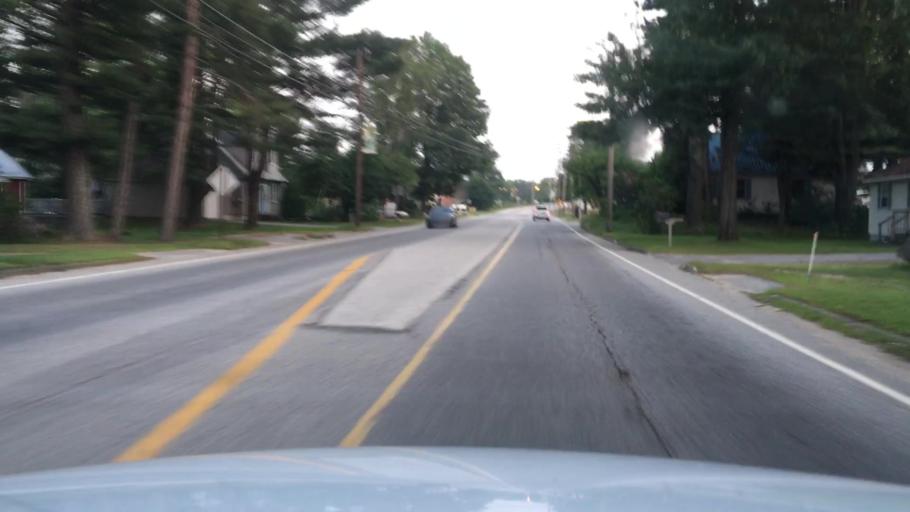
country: US
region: Maine
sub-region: Oxford County
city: Bethel
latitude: 44.4140
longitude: -70.7962
